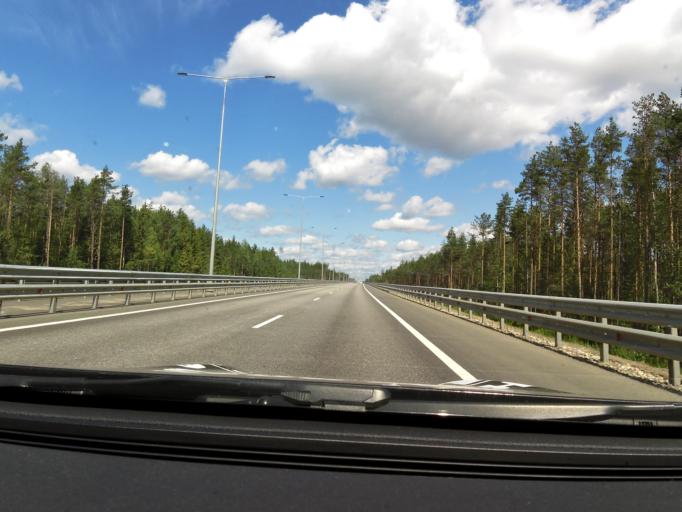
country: RU
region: Tverskaya
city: Krasnomayskiy
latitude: 57.6412
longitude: 34.2356
